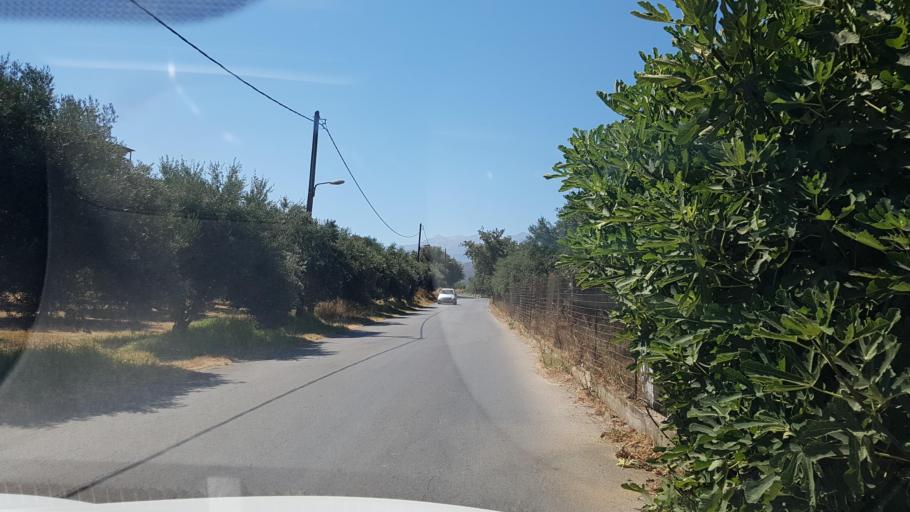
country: GR
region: Crete
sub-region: Nomos Chanias
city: Daratsos
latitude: 35.5029
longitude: 23.9899
